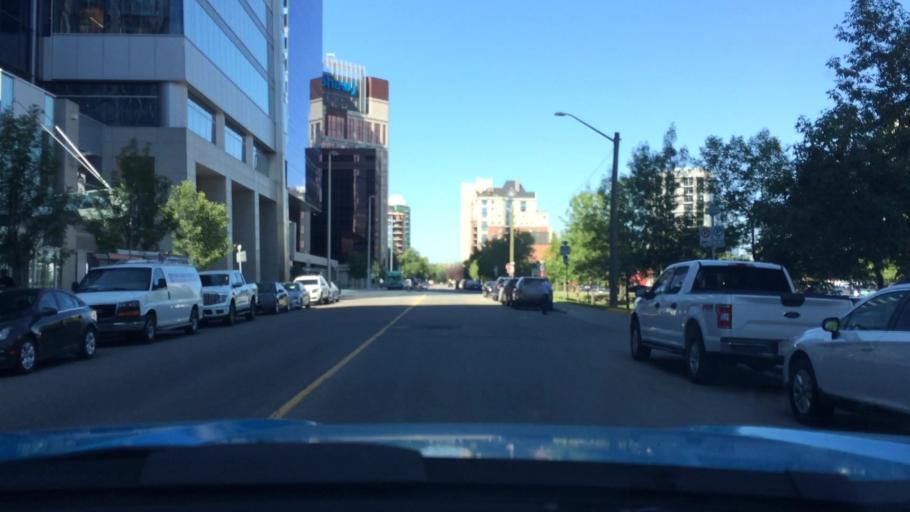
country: CA
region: Alberta
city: Calgary
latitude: 51.0515
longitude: -114.0721
